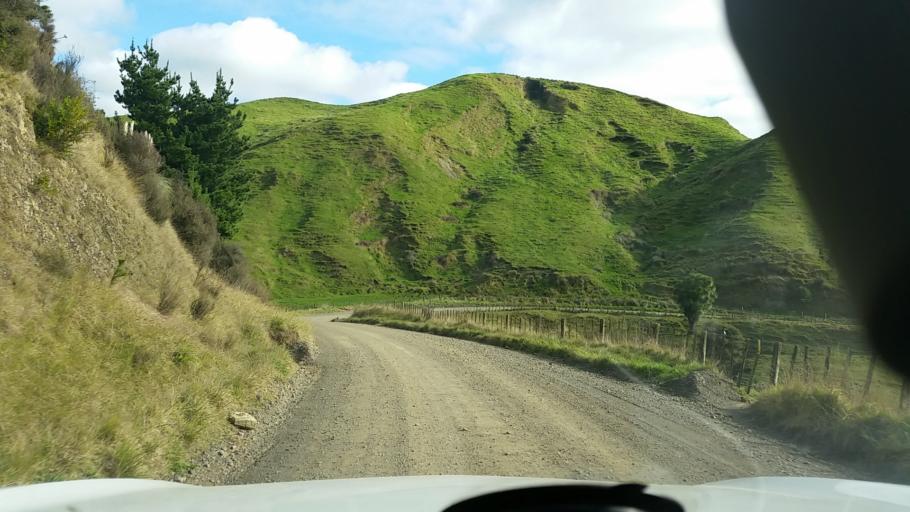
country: NZ
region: Hawke's Bay
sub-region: Napier City
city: Napier
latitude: -39.1112
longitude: 176.8943
